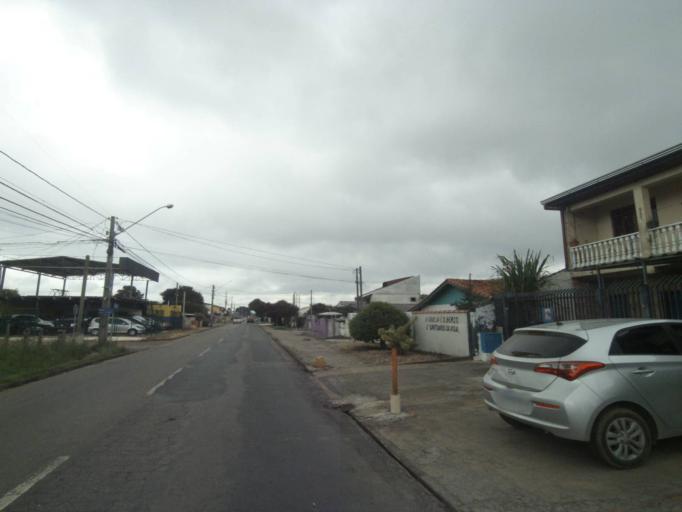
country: BR
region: Parana
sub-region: Pinhais
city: Pinhais
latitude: -25.4432
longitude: -49.1790
